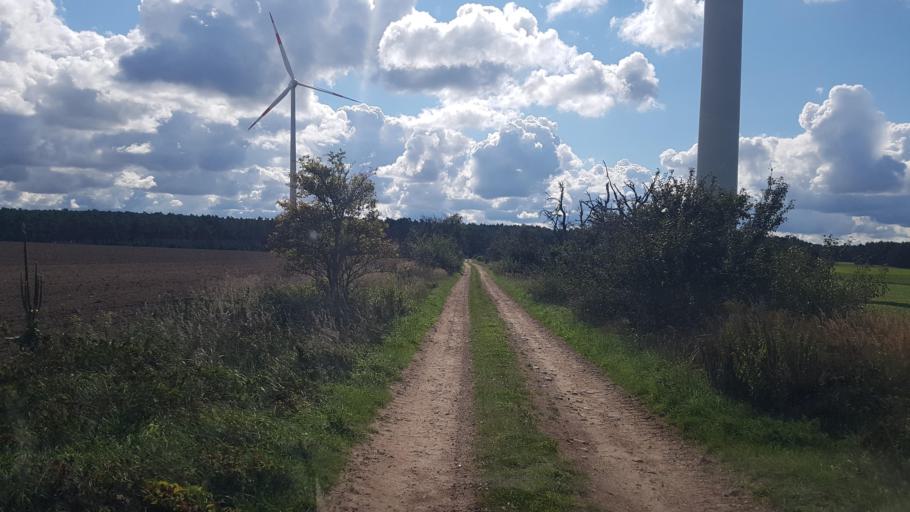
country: DE
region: Brandenburg
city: Niemegk
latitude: 52.0783
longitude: 12.7307
